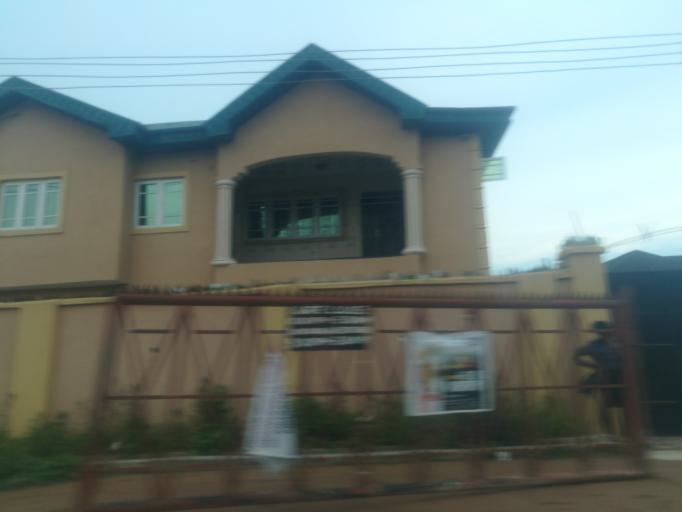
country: NG
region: Oyo
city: Ibadan
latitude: 7.3507
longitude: 3.8213
